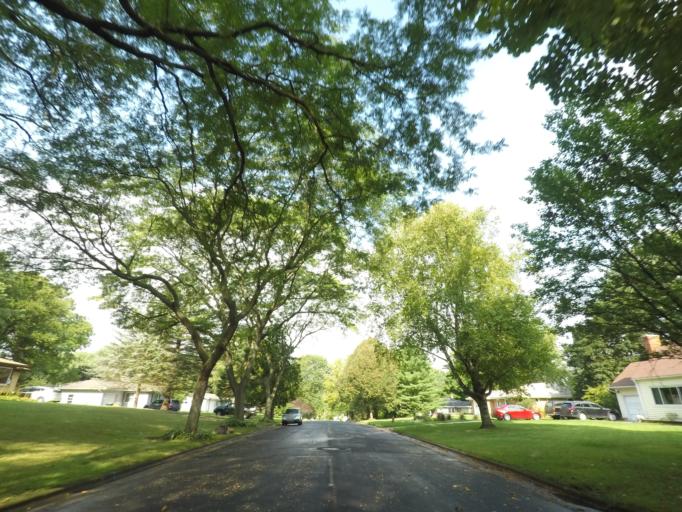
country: US
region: Wisconsin
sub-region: Dane County
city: Shorewood Hills
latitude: 43.0422
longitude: -89.4669
